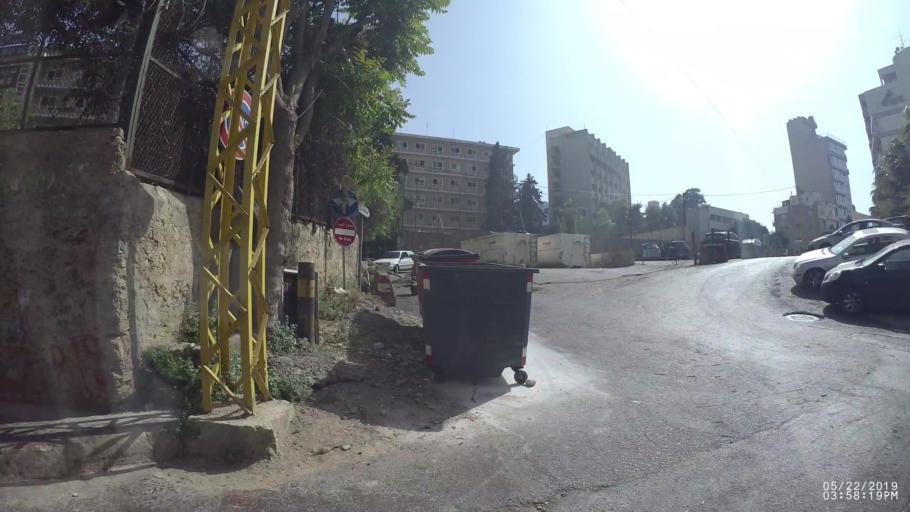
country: LB
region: Beyrouth
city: Ra's Bayrut
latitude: 33.9011
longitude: 35.4857
